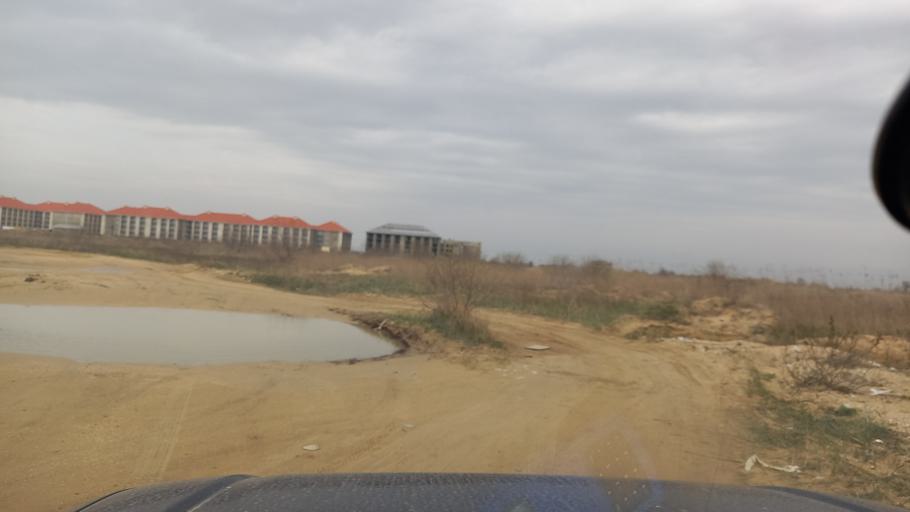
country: RU
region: Krasnodarskiy
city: Vityazevo
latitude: 44.9920
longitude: 37.2387
